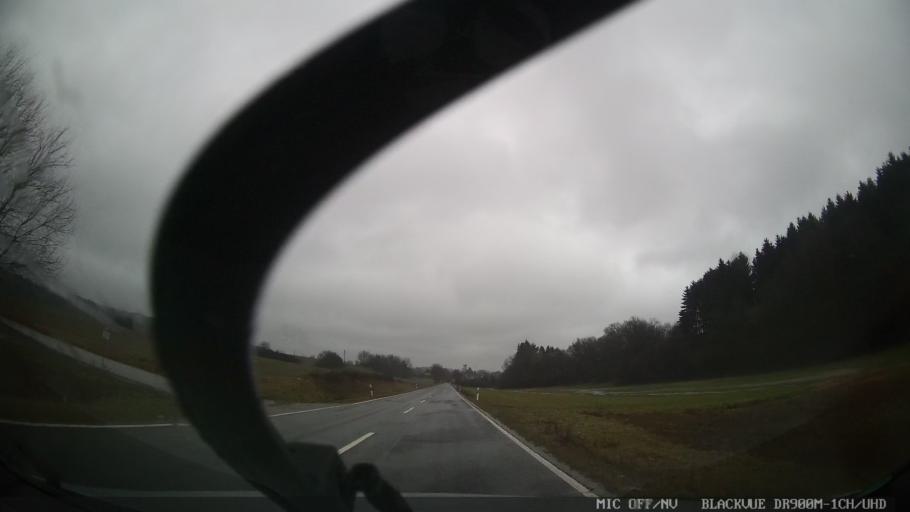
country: DE
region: Rheinland-Pfalz
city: Achtelsbach
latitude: 49.6207
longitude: 7.0818
